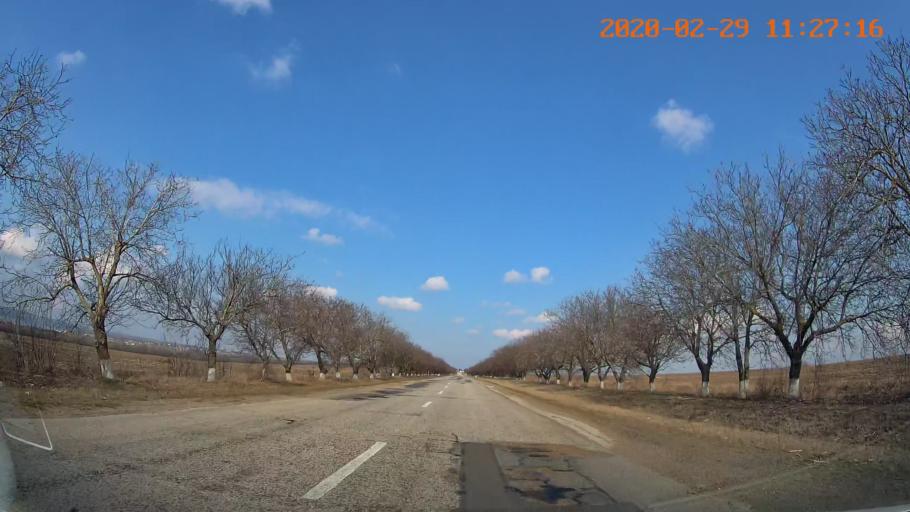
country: MD
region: Telenesti
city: Cocieri
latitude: 47.4656
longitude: 29.1432
